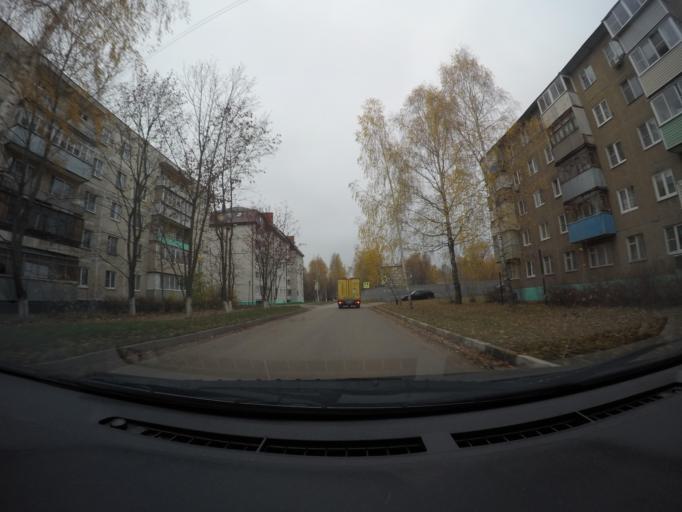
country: RU
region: Moskovskaya
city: Rechitsy
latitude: 55.5852
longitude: 38.4967
